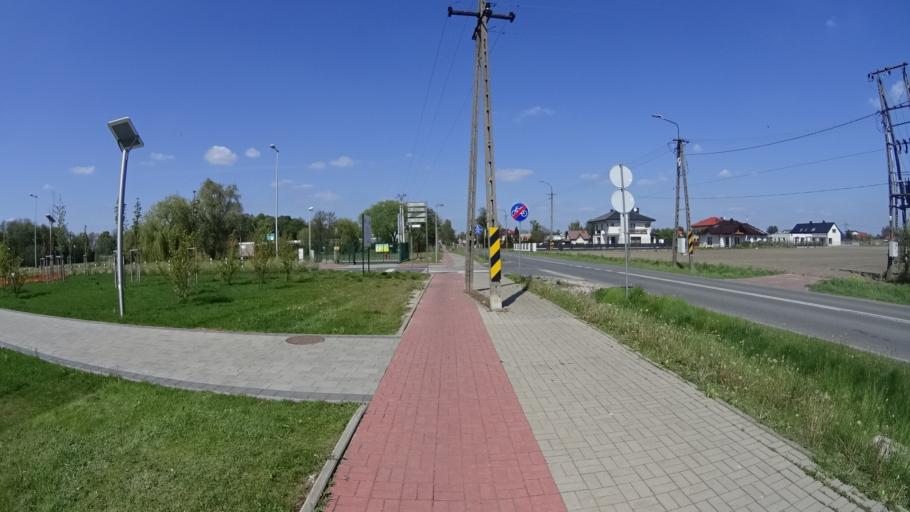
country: PL
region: Masovian Voivodeship
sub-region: Powiat warszawski zachodni
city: Stare Babice
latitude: 52.2482
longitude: 20.8201
